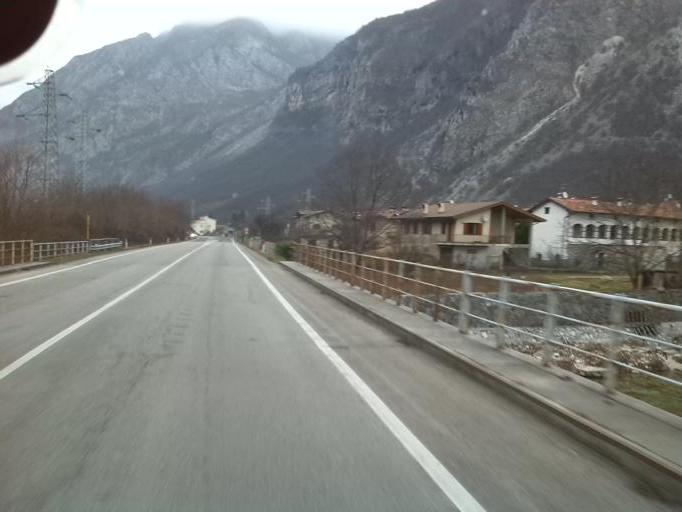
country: IT
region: Friuli Venezia Giulia
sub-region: Provincia di Udine
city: Venzone
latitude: 46.3361
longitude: 13.1385
